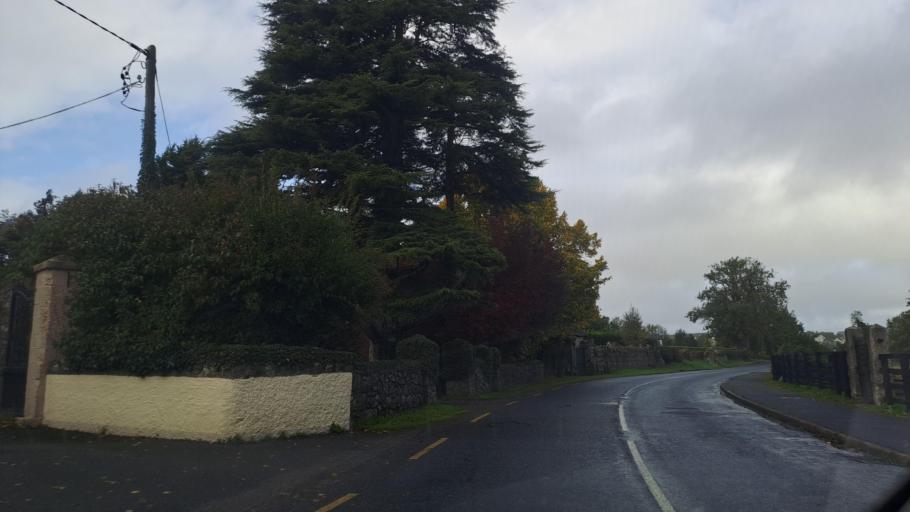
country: IE
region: Ulster
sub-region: County Monaghan
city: Carrickmacross
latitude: 53.9610
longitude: -6.7126
